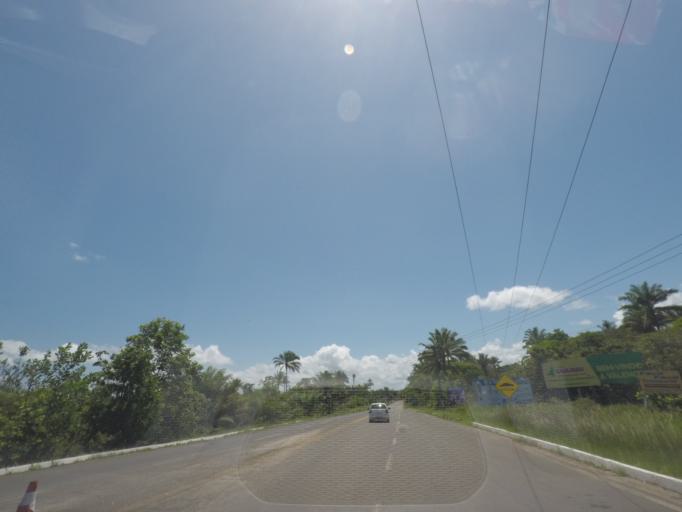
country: BR
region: Bahia
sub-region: Valenca
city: Valenca
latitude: -13.3239
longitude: -39.0406
